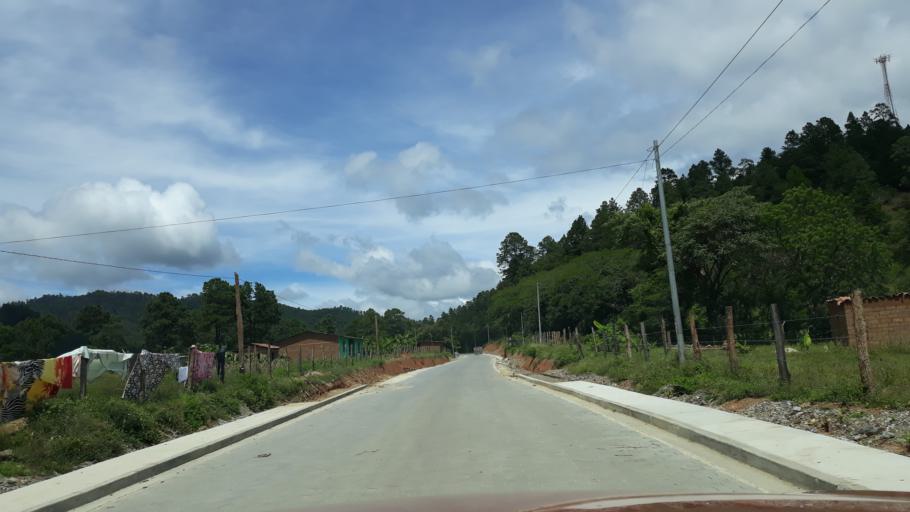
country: HN
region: El Paraiso
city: Santa Cruz
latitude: 13.7359
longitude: -86.6247
